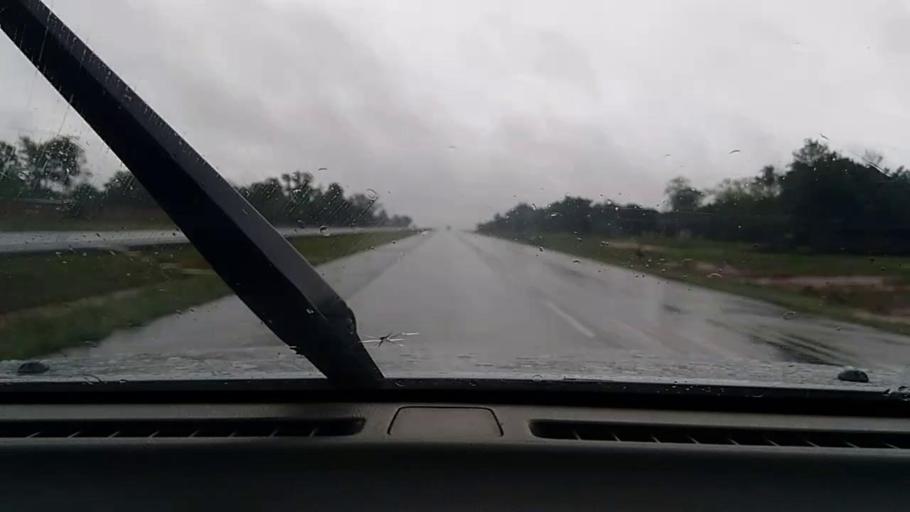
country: PY
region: Caaguazu
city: Repatriacion
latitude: -25.4663
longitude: -55.9393
